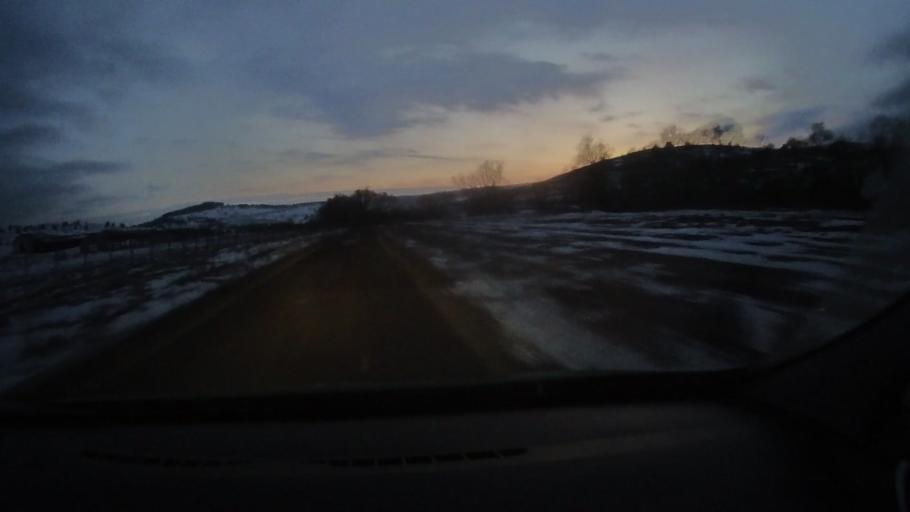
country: RO
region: Harghita
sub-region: Comuna Darjiu
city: Darjiu
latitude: 46.1564
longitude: 25.2026
